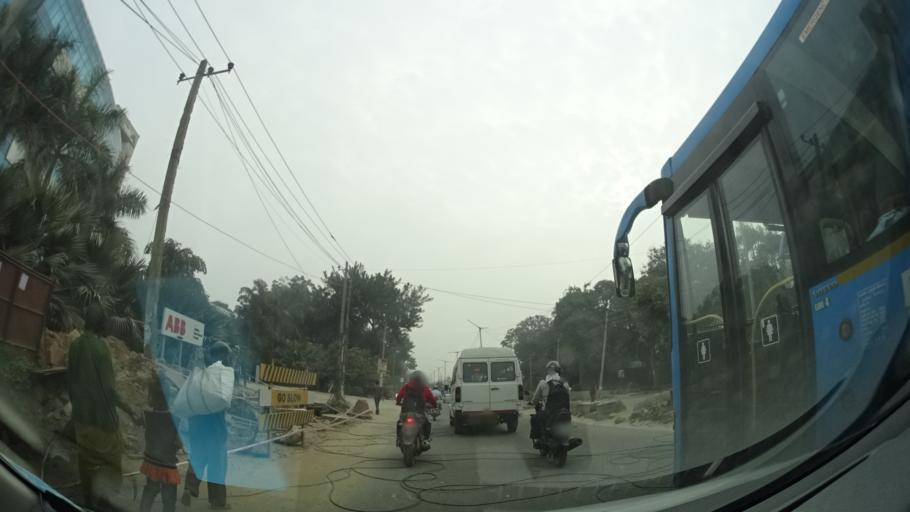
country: IN
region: Karnataka
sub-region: Bangalore Urban
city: Bangalore
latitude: 12.9932
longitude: 77.7054
